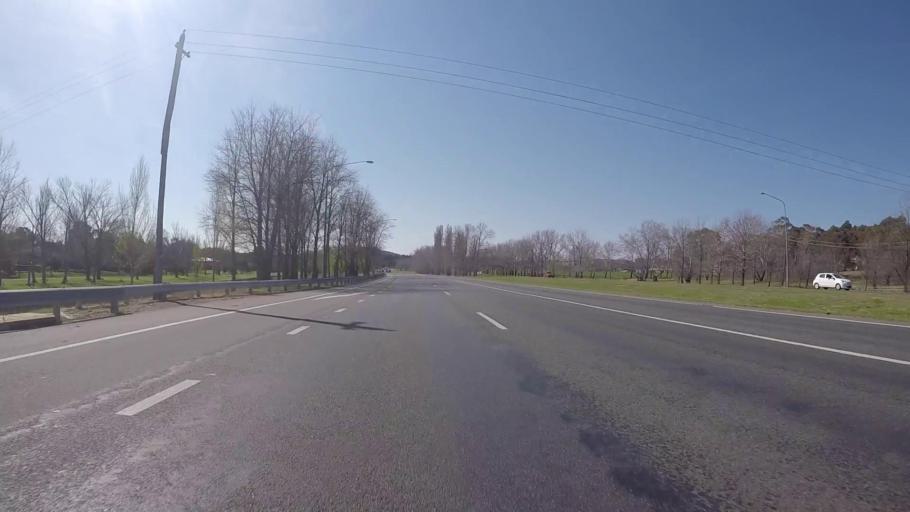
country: AU
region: Australian Capital Territory
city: Forrest
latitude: -35.3234
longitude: 149.0881
